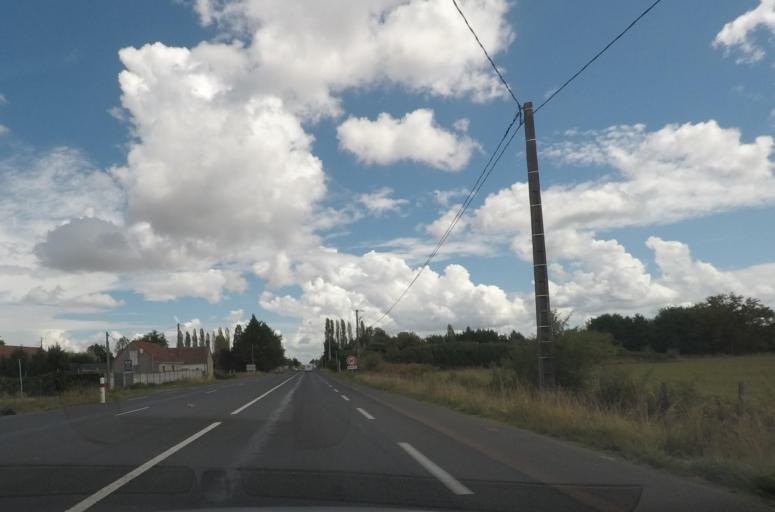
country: FR
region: Pays de la Loire
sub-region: Departement de la Sarthe
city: Spay
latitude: 47.8977
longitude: 0.1554
